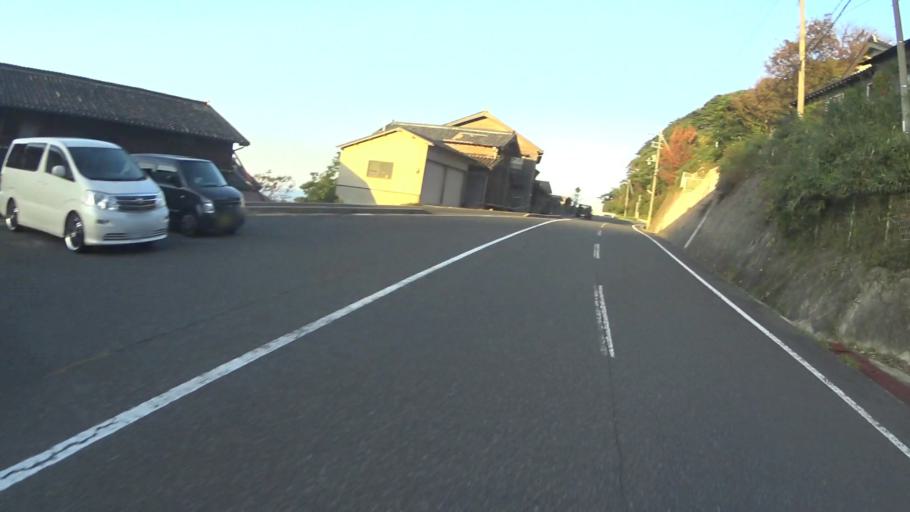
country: JP
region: Hyogo
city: Toyooka
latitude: 35.6898
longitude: 134.9954
